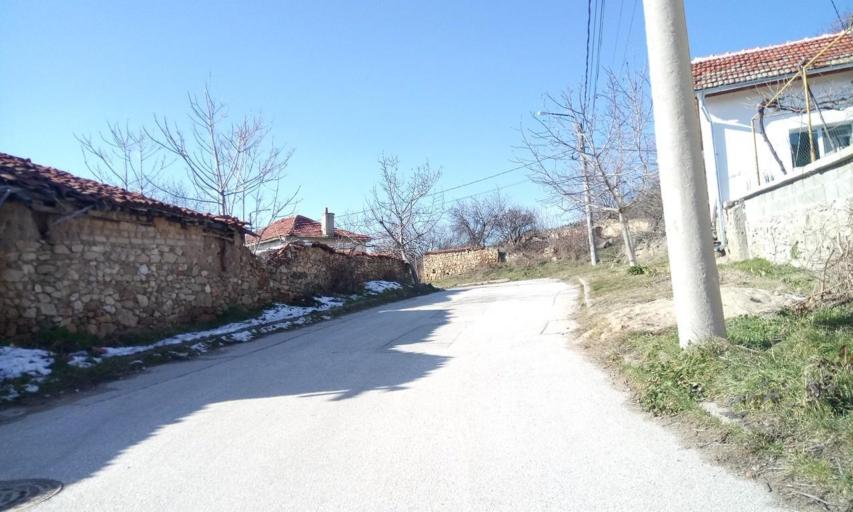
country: BG
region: Plovdiv
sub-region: Obshtina Khisarya
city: Khisarya
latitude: 42.5235
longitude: 24.7194
